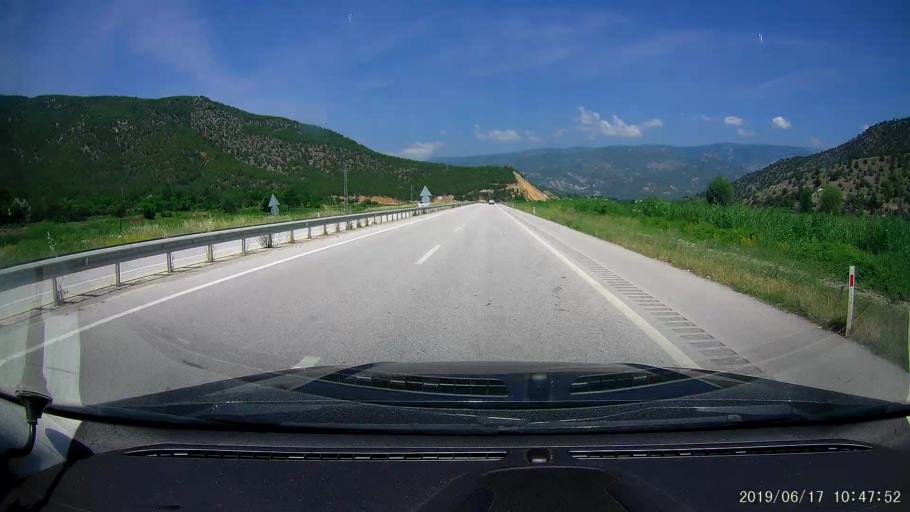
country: TR
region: Corum
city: Hacihamza
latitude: 41.0813
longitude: 34.4408
